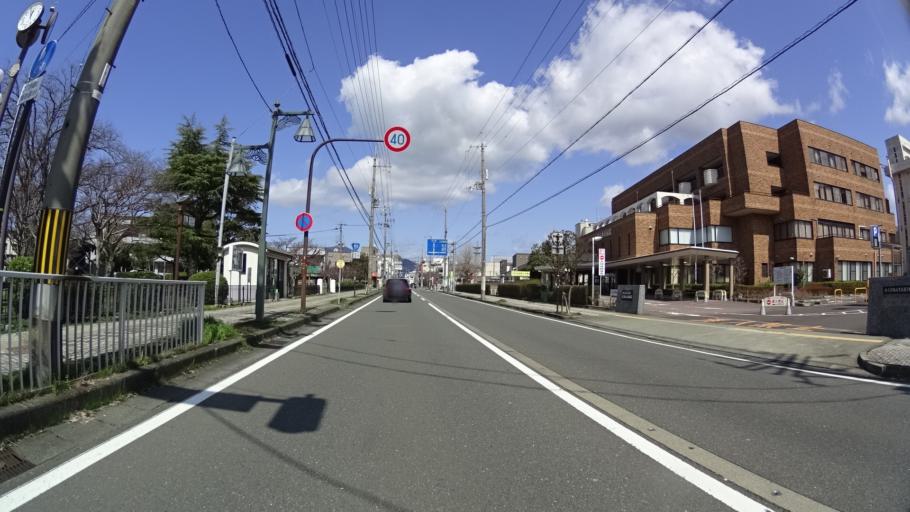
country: JP
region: Fukui
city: Obama
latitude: 35.4939
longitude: 135.7456
